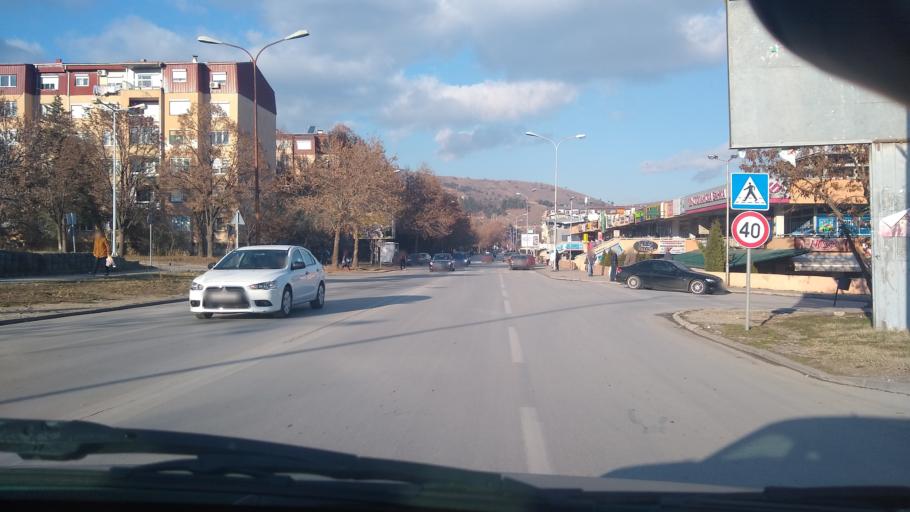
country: MK
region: Bitola
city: Bitola
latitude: 41.0267
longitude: 21.3134
